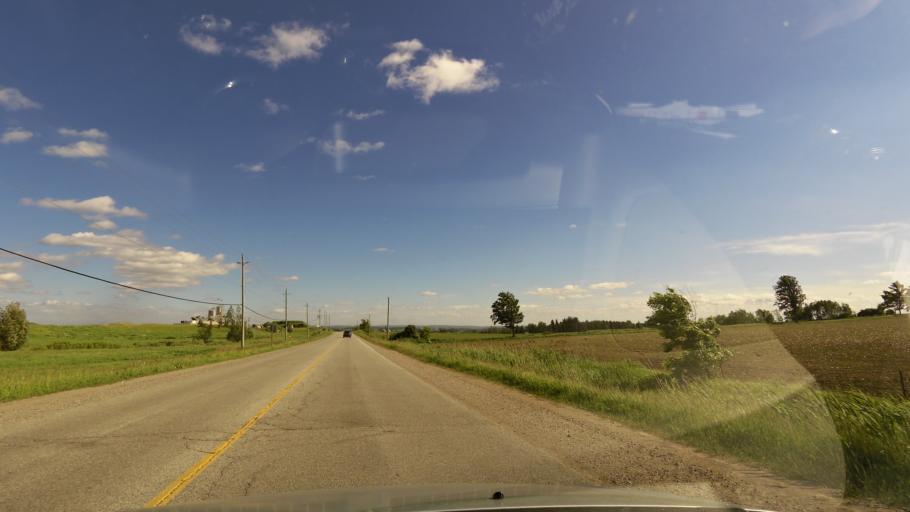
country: CA
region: Ontario
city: Bradford West Gwillimbury
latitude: 44.1255
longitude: -79.6067
